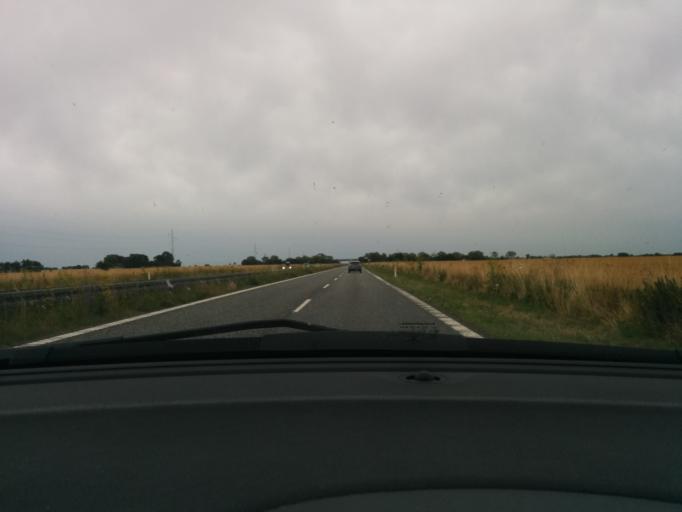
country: DK
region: Zealand
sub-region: Lolland Kommune
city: Rodby
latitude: 54.6915
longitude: 11.4070
